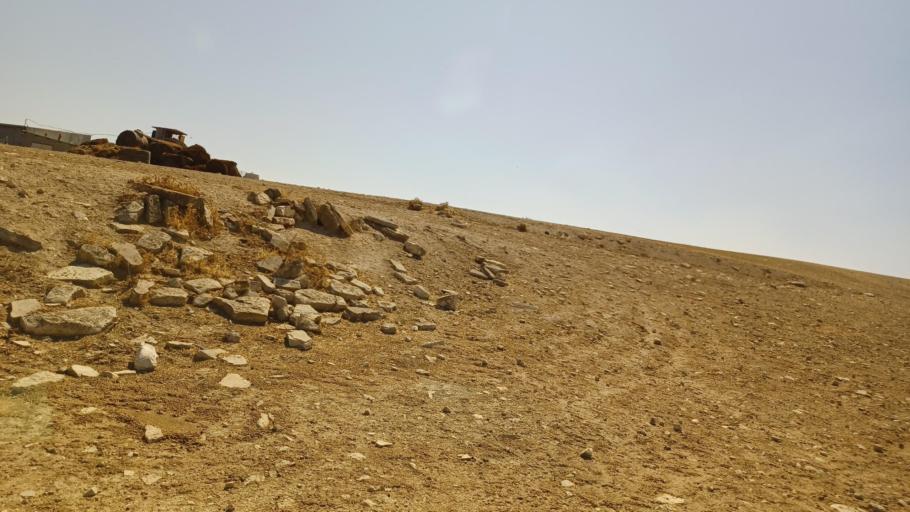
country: CY
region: Larnaka
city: Athienou
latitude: 35.0432
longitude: 33.5296
